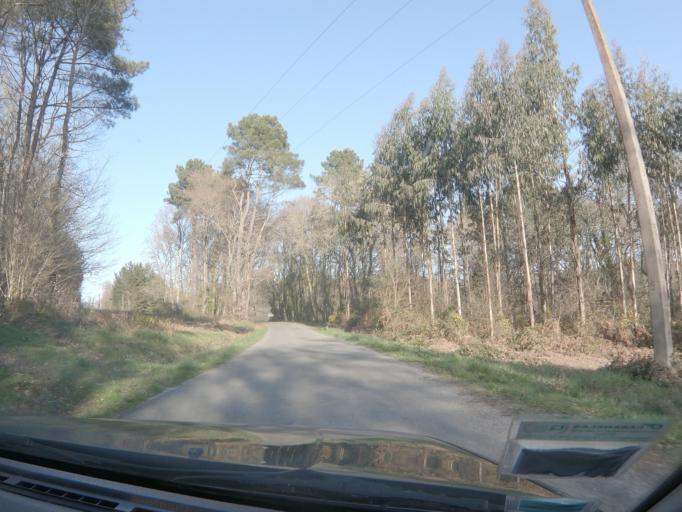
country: ES
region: Galicia
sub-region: Provincia de Lugo
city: Corgo
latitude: 42.9398
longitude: -7.4428
